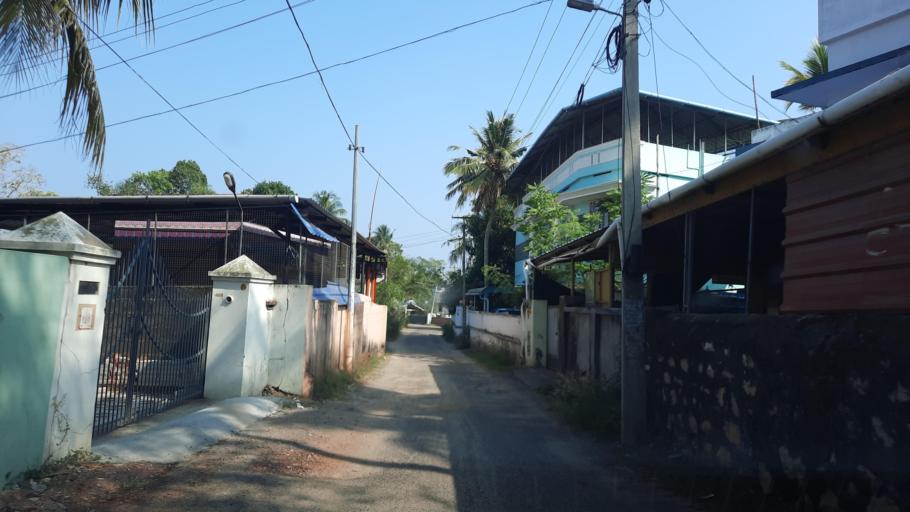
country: IN
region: Kerala
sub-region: Thiruvananthapuram
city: Thiruvananthapuram
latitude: 8.5604
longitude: 76.9235
